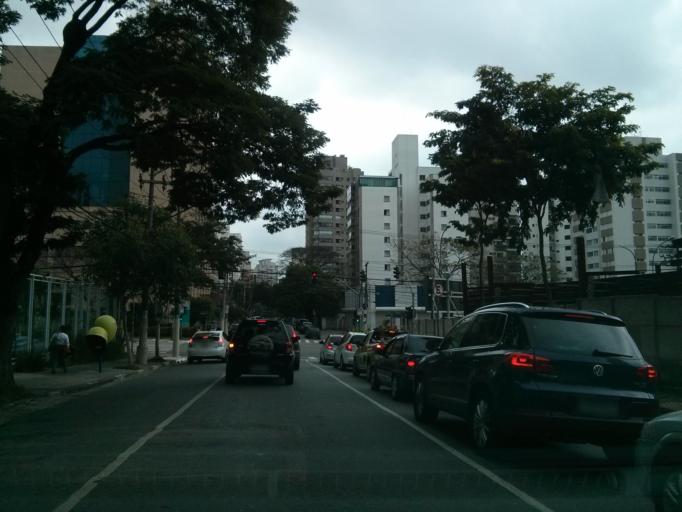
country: BR
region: Sao Paulo
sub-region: Sao Paulo
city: Sao Paulo
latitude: -23.6020
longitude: -46.6600
